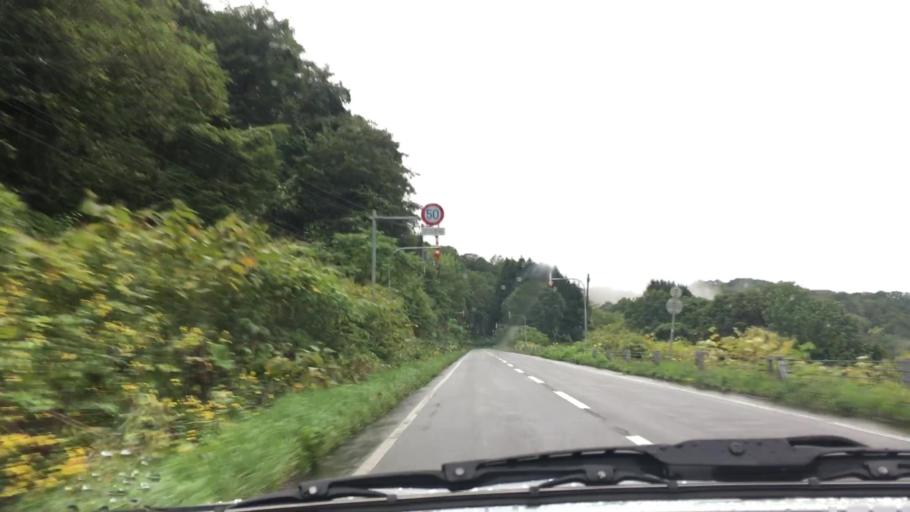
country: JP
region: Hokkaido
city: Niseko Town
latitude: 42.6321
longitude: 140.7263
